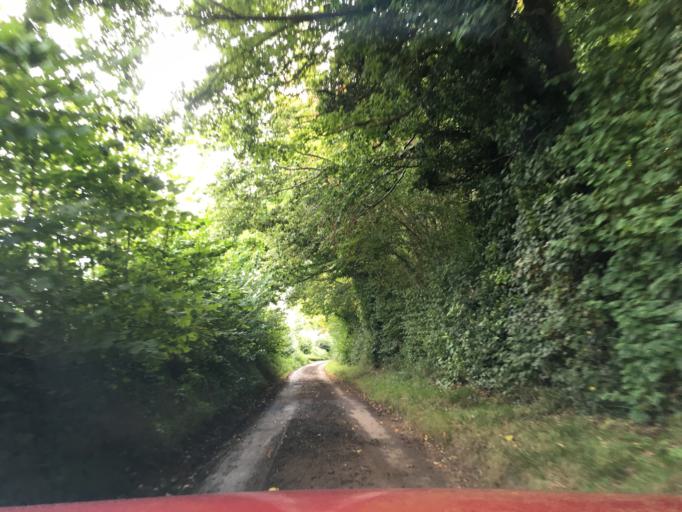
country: GB
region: England
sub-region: South Gloucestershire
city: Falfield
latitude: 51.6104
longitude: -2.4560
